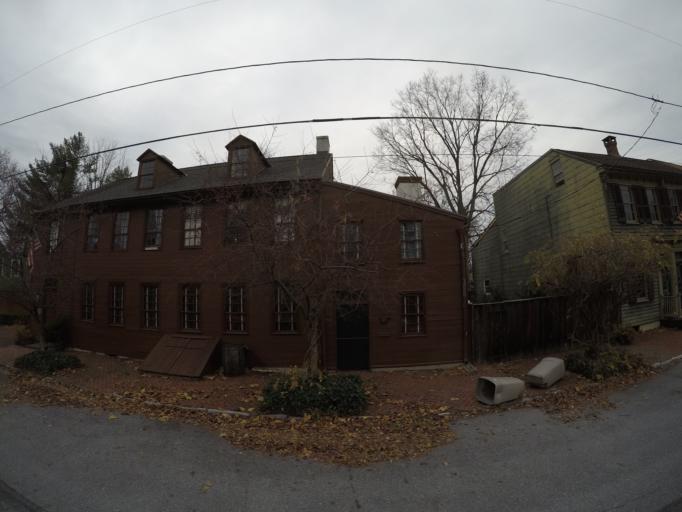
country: US
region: Pennsylvania
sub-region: Lancaster County
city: Marietta
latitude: 40.0547
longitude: -76.5588
